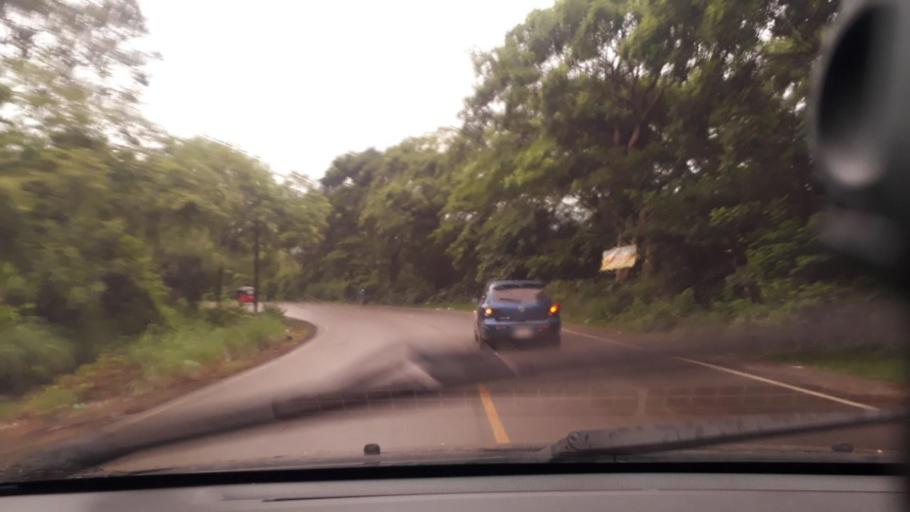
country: GT
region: Jutiapa
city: Atescatempa
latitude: 14.1990
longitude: -89.6790
